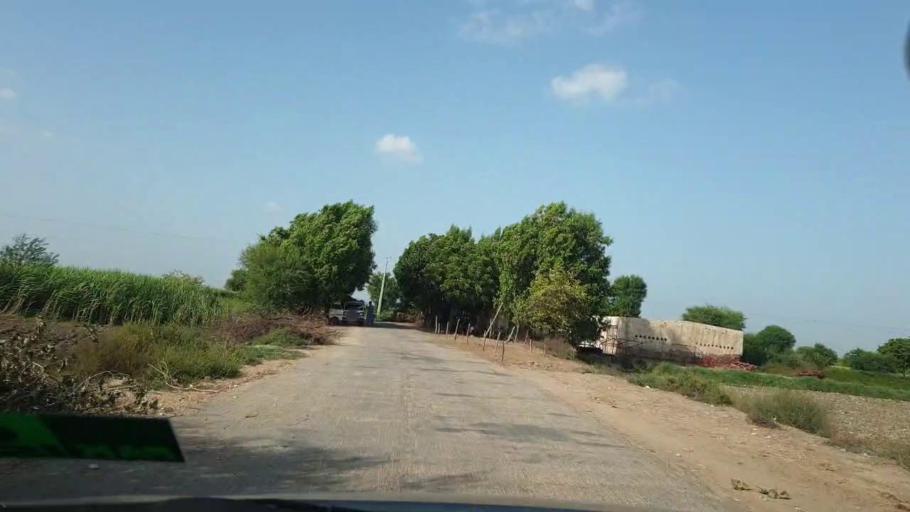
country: PK
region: Sindh
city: Tando Bago
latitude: 24.7214
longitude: 69.1957
